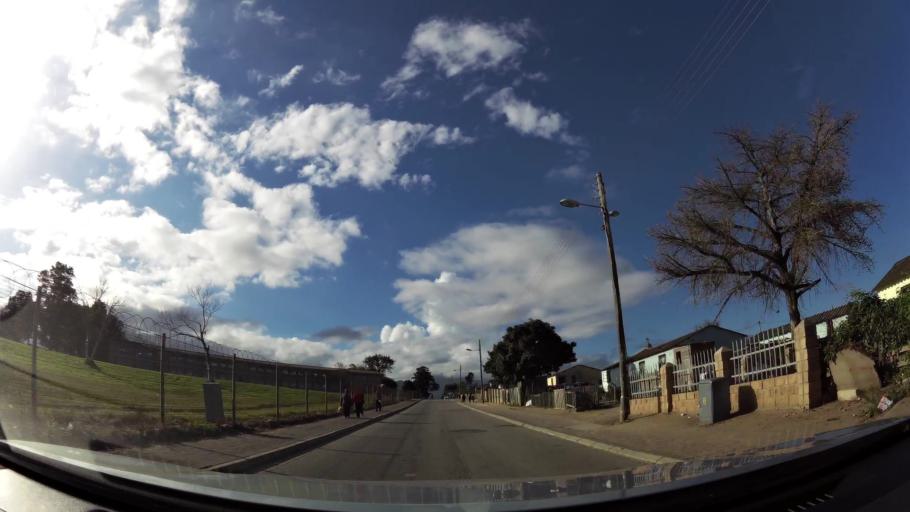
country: ZA
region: Western Cape
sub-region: Eden District Municipality
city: George
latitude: -33.9769
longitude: 22.4783
